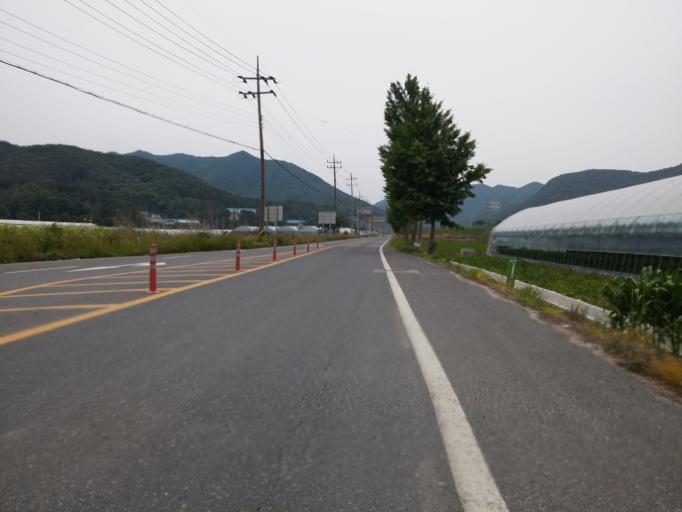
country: KR
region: Chungcheongbuk-do
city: Okcheon
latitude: 36.2703
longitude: 127.5253
